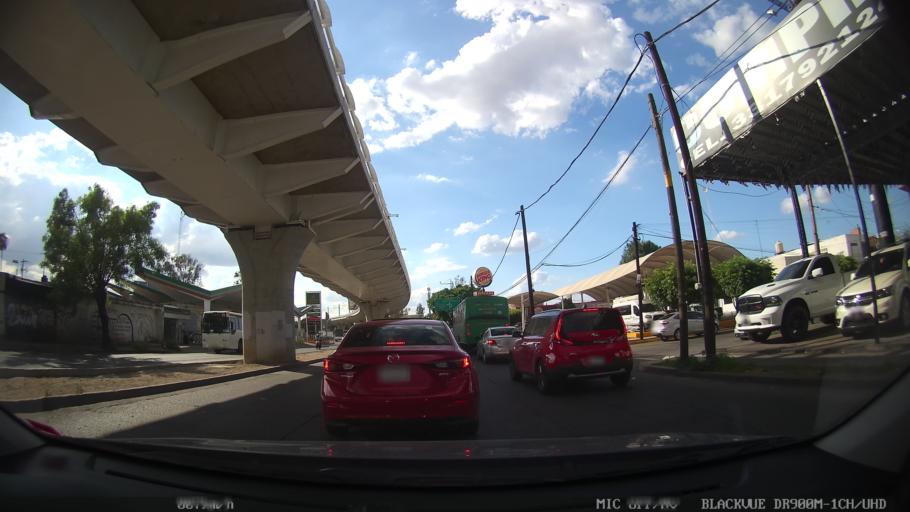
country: MX
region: Jalisco
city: Tlaquepaque
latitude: 20.6472
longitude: -103.3054
